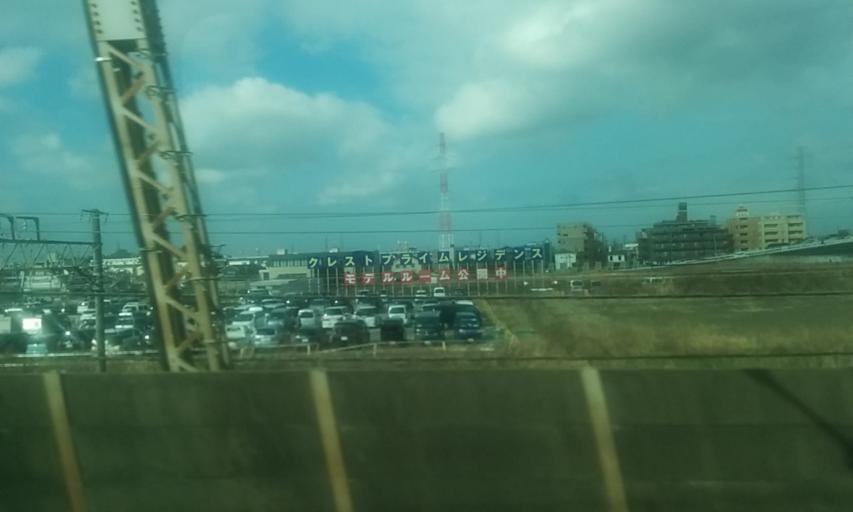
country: JP
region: Kanagawa
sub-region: Kawasaki-shi
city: Kawasaki
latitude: 35.5412
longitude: 139.6753
